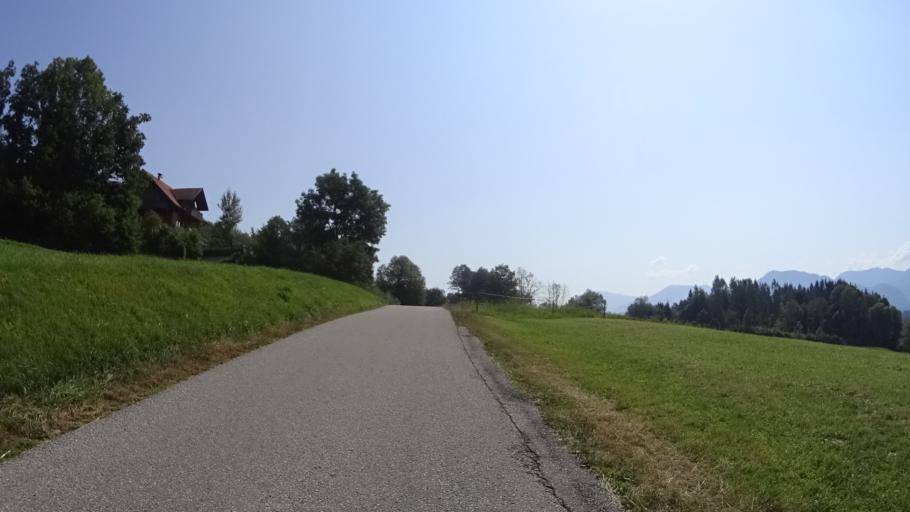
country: AT
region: Carinthia
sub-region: Politischer Bezirk Volkermarkt
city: Gallizien
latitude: 46.5634
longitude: 14.5436
